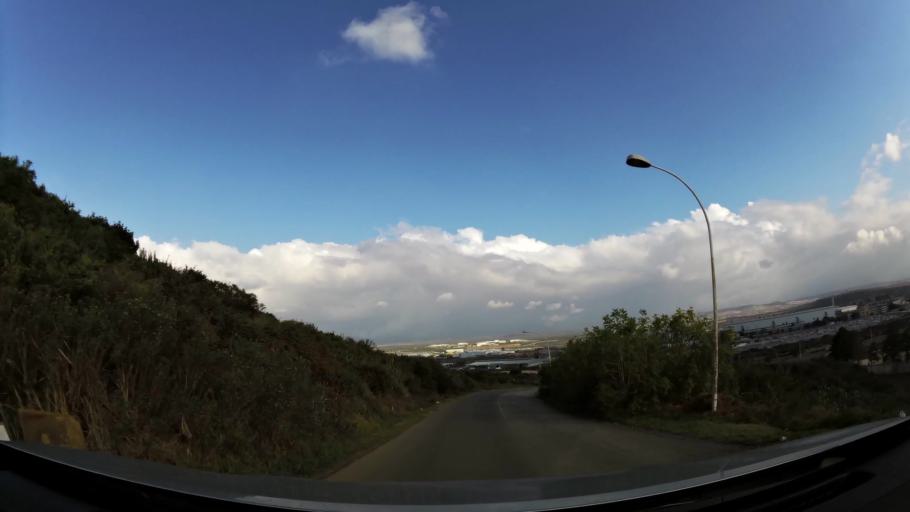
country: ZA
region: Eastern Cape
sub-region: Nelson Mandela Bay Metropolitan Municipality
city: Uitenhage
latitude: -33.7787
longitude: 25.4252
